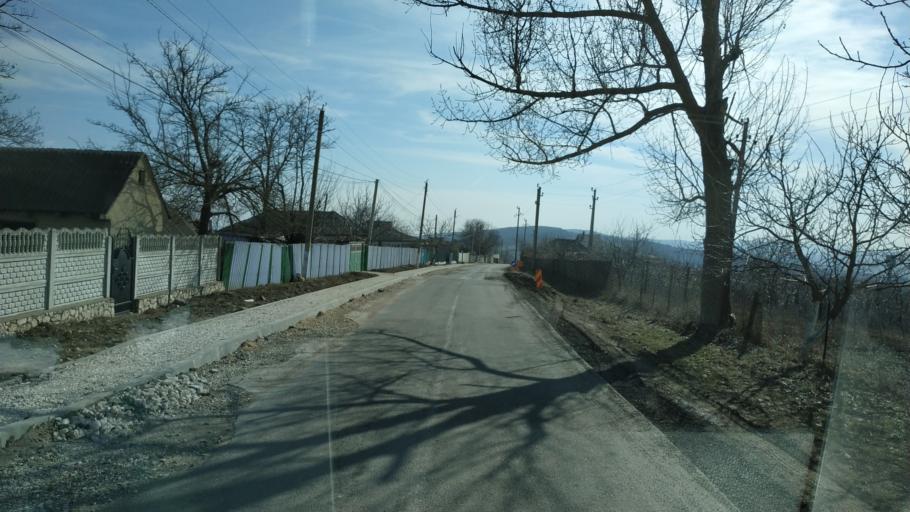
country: MD
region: Nisporeni
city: Nisporeni
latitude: 47.2023
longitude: 28.0607
